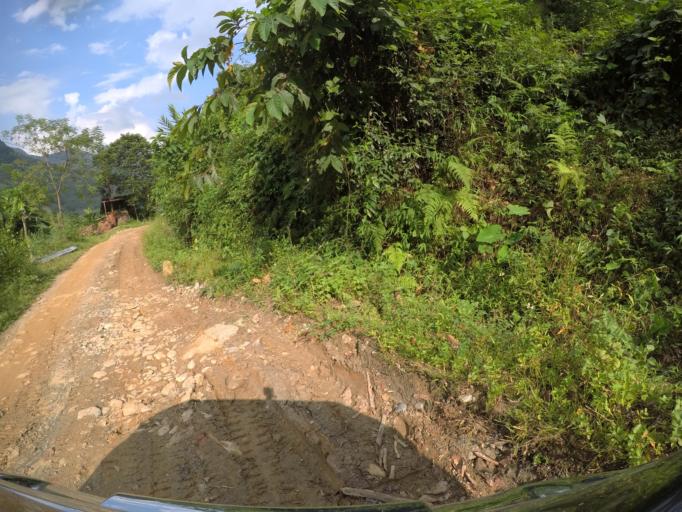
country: VN
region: Yen Bai
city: Son Thinh
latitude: 21.6791
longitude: 104.5892
